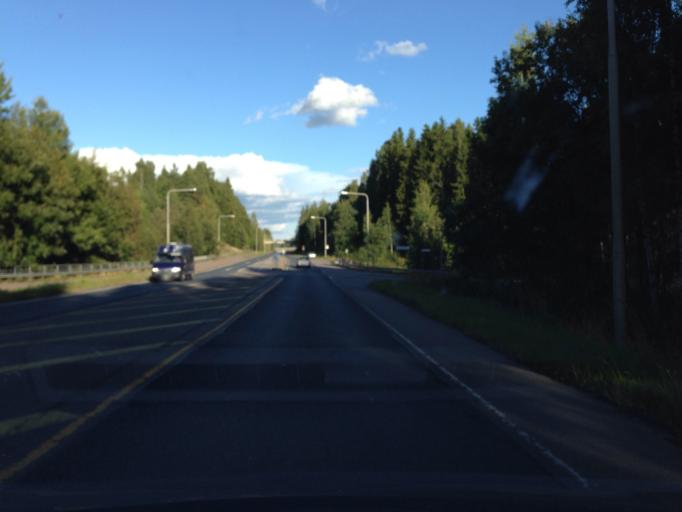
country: FI
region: Uusimaa
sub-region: Helsinki
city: Vantaa
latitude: 60.3473
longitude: 25.0568
